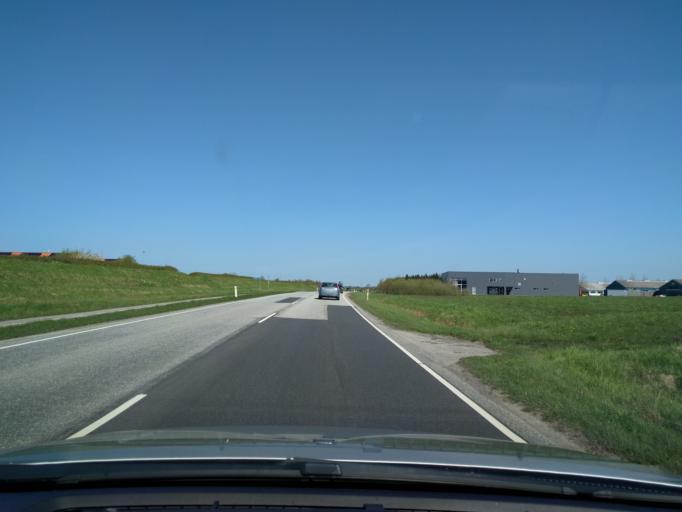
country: DK
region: Central Jutland
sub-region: Ringkobing-Skjern Kommune
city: Ringkobing
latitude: 56.0924
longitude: 8.2777
